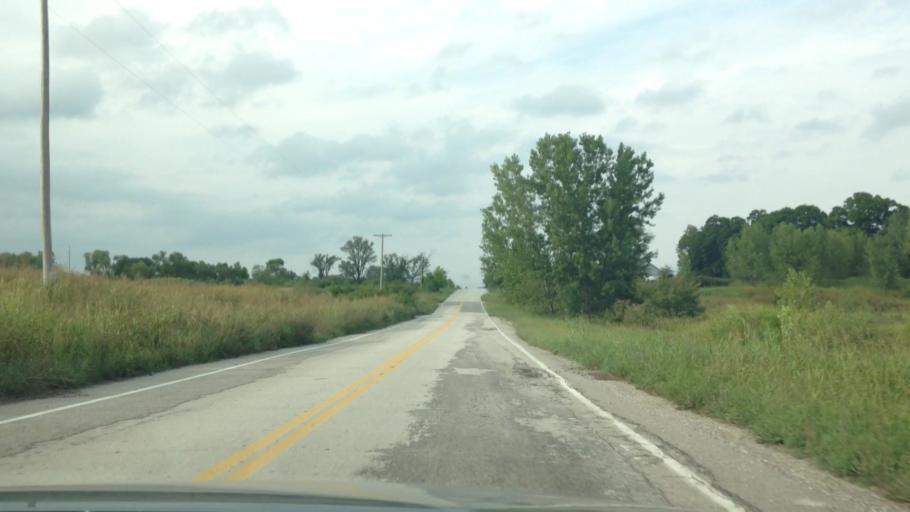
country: US
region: Missouri
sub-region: Clay County
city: Smithville
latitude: 39.3524
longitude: -94.6790
